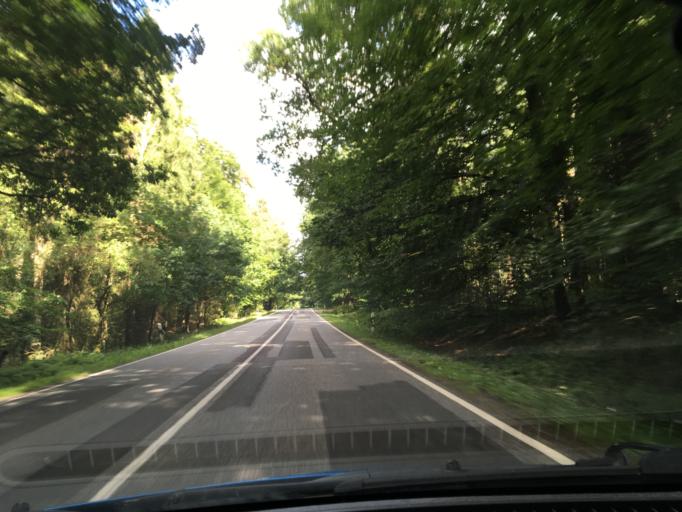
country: DE
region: Mecklenburg-Vorpommern
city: Lubtheen
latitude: 53.3995
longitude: 11.0300
